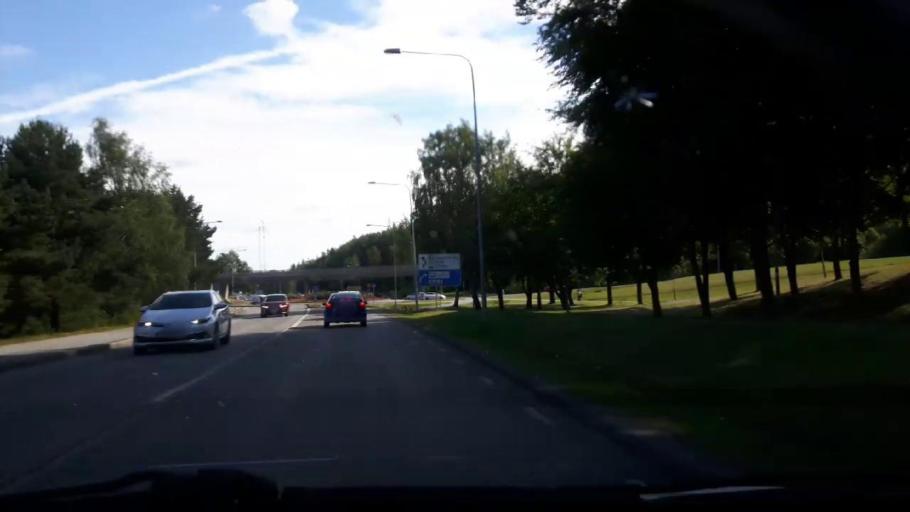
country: SE
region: Stockholm
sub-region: Sodertalje Kommun
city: Soedertaelje
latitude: 59.1779
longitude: 17.6330
